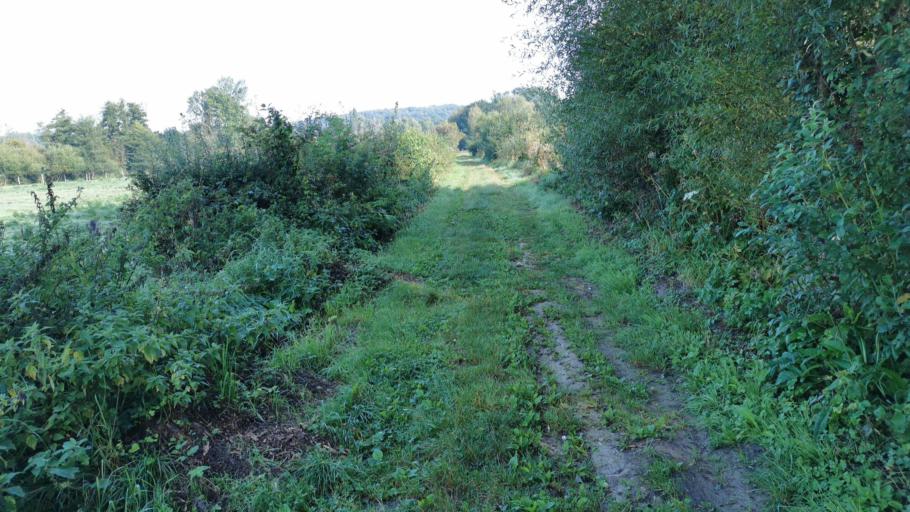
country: FR
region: Picardie
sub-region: Departement de la Somme
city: Pont-Remy
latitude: 50.0369
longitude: 1.9495
